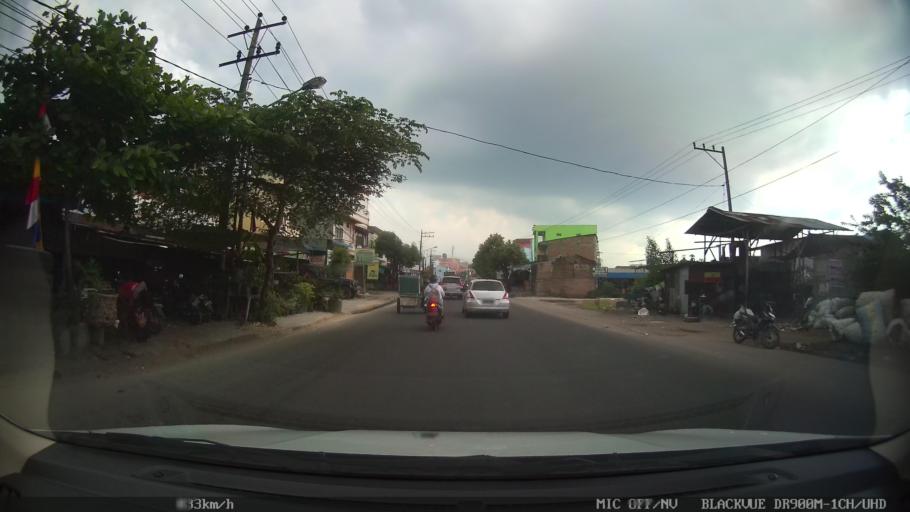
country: ID
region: North Sumatra
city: Sunggal
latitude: 3.5221
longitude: 98.6196
